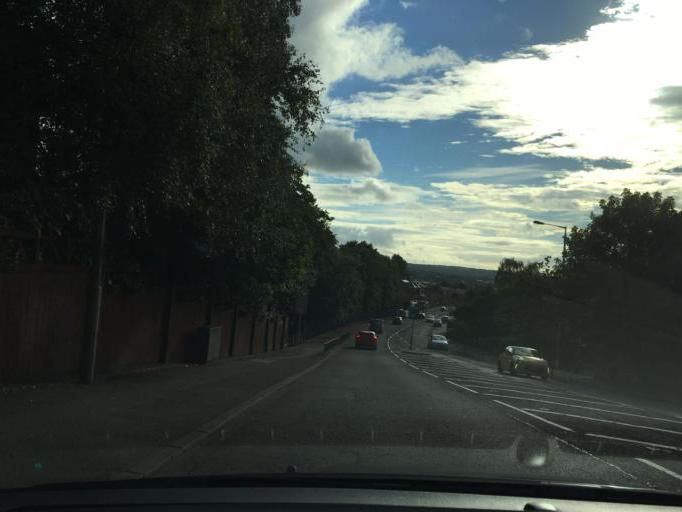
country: GB
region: Scotland
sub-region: North Lanarkshire
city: Motherwell
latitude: 55.7881
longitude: -3.9983
